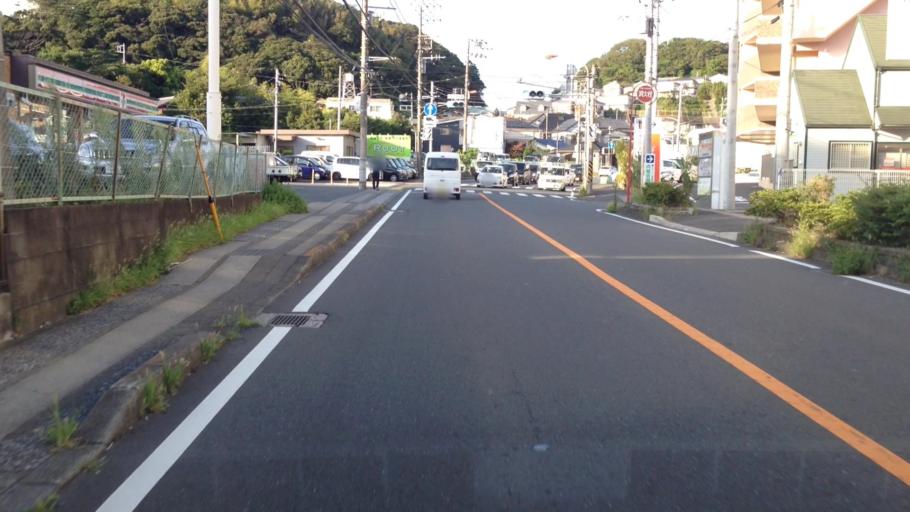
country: JP
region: Kanagawa
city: Yokosuka
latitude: 35.2292
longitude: 139.6522
